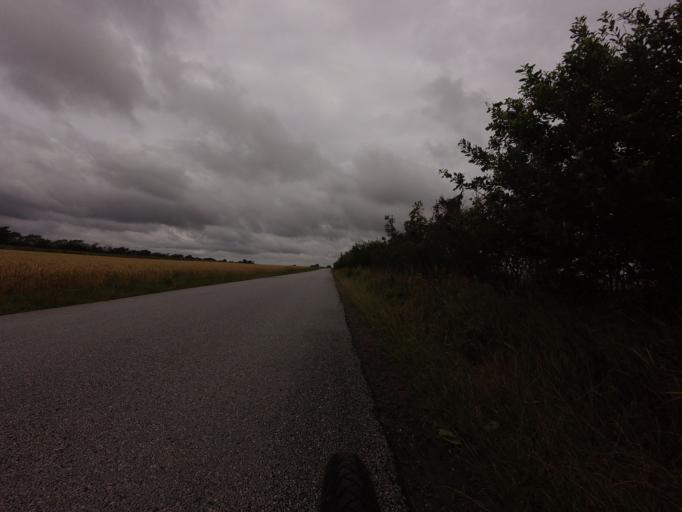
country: DK
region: North Denmark
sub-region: Bronderslev Kommune
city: Bronderslev
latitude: 57.3012
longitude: 9.8044
